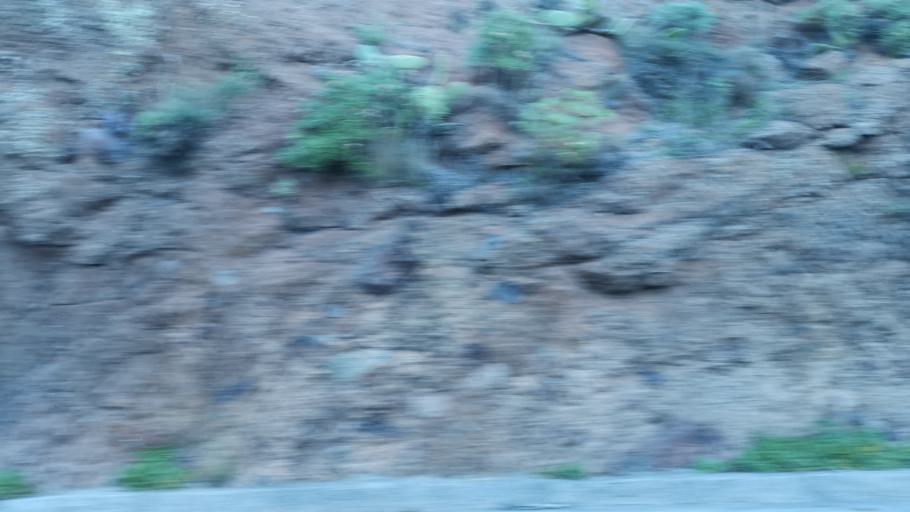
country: ES
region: Canary Islands
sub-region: Provincia de Santa Cruz de Tenerife
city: Alajero
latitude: 28.0815
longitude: -17.2442
